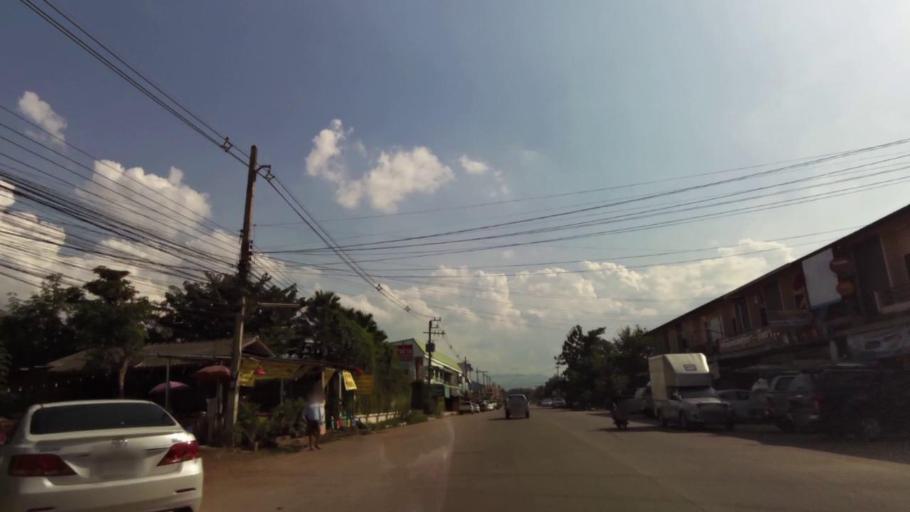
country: TH
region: Phrae
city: Phrae
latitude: 18.1230
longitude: 100.1530
